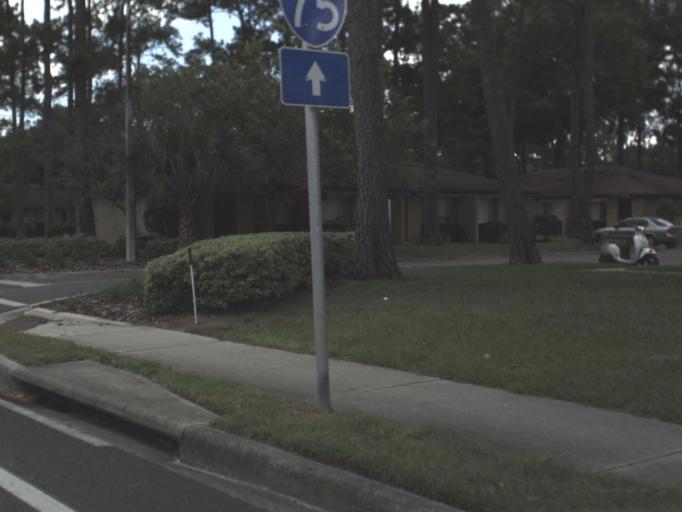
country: US
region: Florida
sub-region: Alachua County
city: Alachua
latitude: 29.6887
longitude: -82.3897
